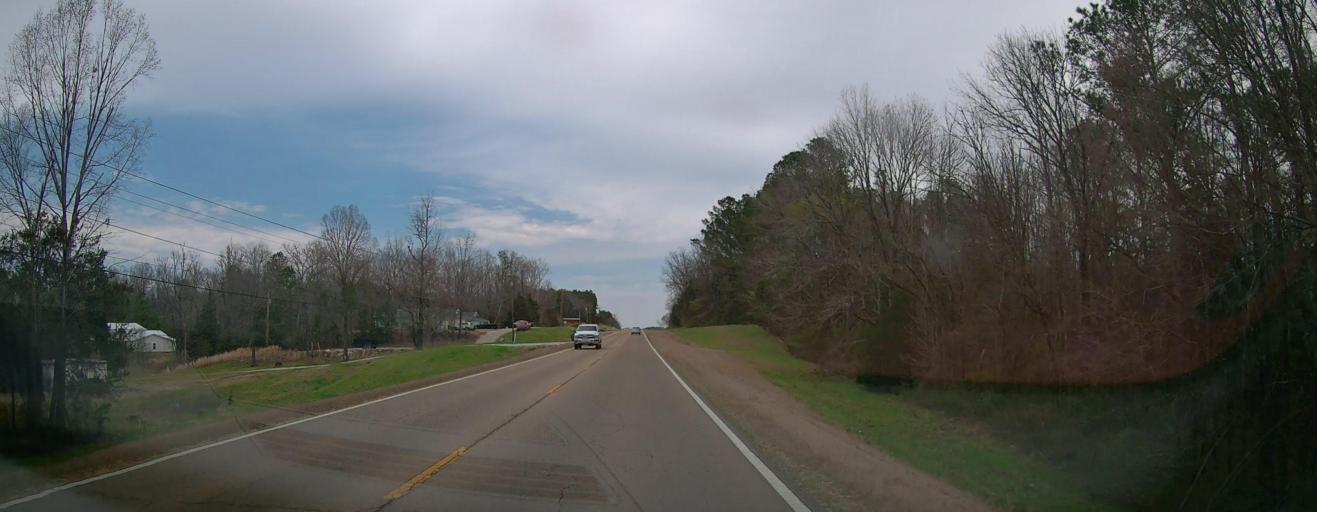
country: US
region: Mississippi
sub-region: Lee County
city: Plantersville
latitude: 34.2659
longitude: -88.6173
